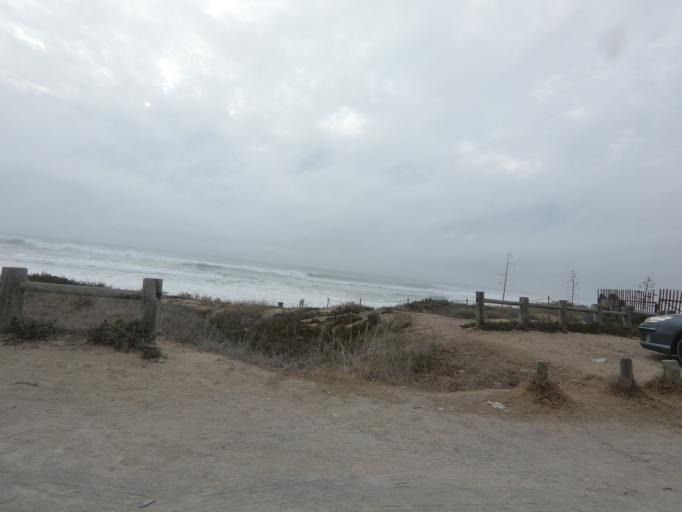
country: PT
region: Setubal
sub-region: Almada
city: Charneca
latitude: 38.5650
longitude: -9.1921
